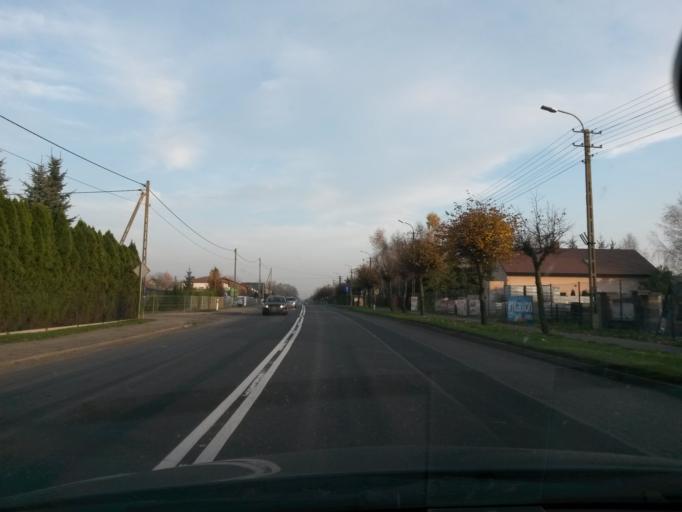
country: PL
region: Lodz Voivodeship
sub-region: Powiat wieruszowski
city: Walichnowy
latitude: 51.2642
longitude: 18.4570
